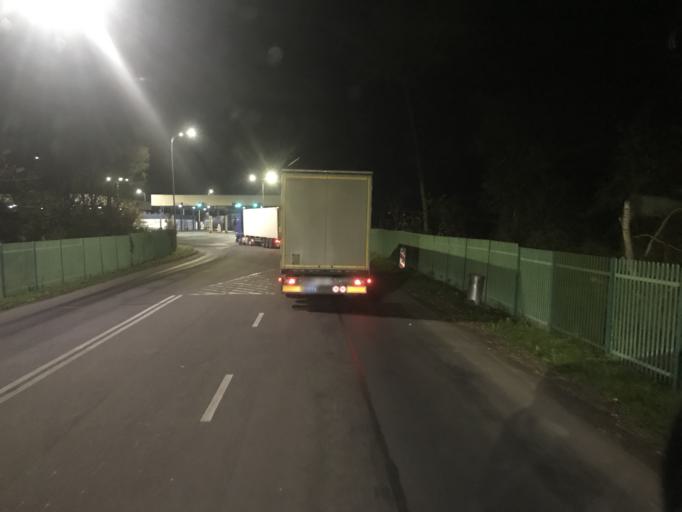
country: PL
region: Lublin Voivodeship
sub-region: Powiat bialski
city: Terespol
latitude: 52.1093
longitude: 23.5604
